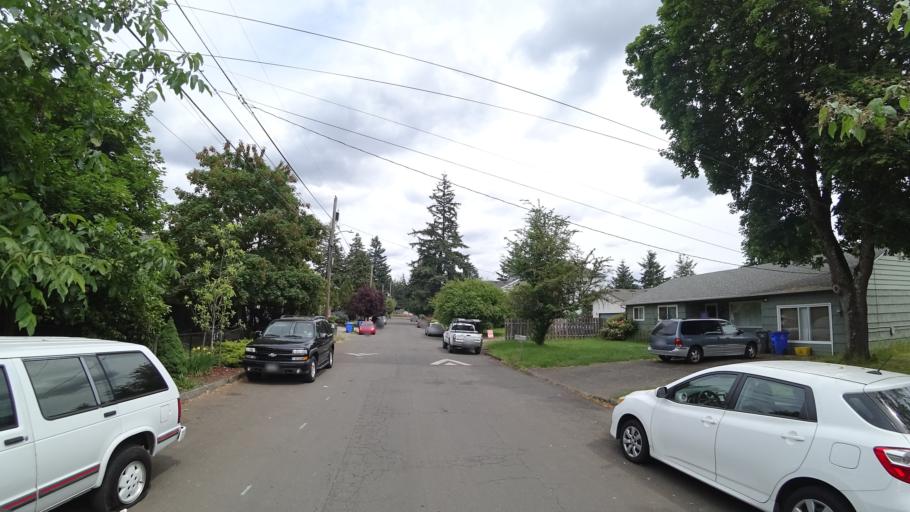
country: US
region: Oregon
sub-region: Multnomah County
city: Lents
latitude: 45.4868
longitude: -122.5407
